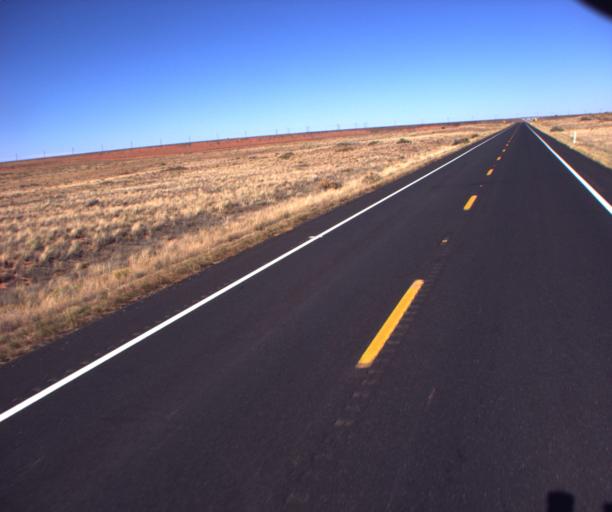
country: US
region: Arizona
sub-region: Coconino County
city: Kaibito
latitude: 36.3839
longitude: -110.8856
